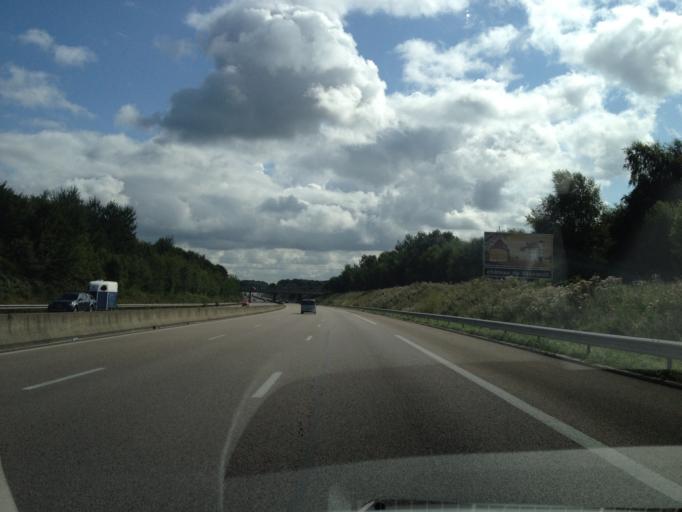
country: FR
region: Haute-Normandie
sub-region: Departement de la Seine-Maritime
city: Grand-Couronne
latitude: 49.3377
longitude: 1.0095
